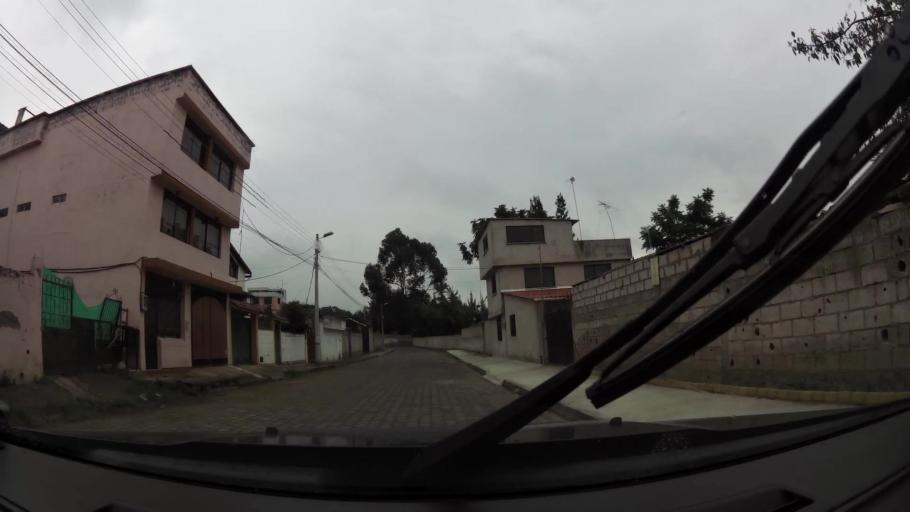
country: EC
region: Pichincha
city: Sangolqui
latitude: -0.2767
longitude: -78.4688
